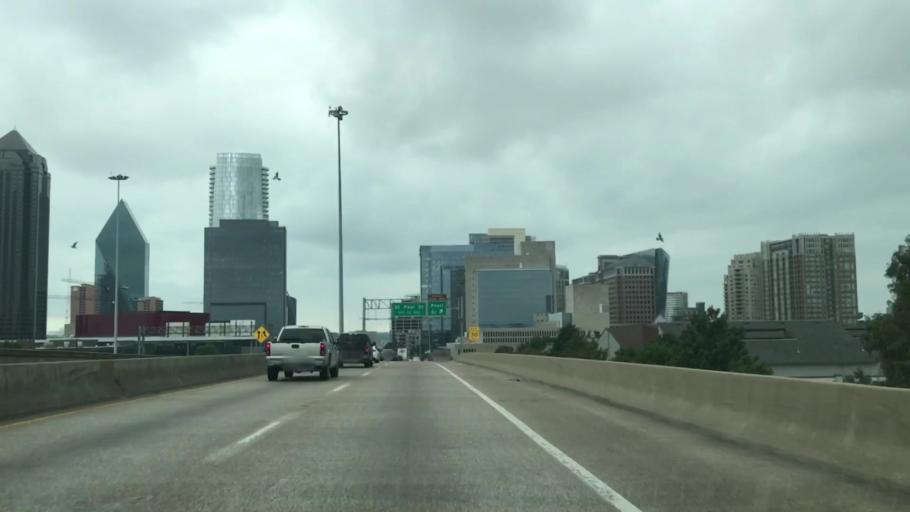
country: US
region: Texas
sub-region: Dallas County
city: Dallas
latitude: 32.7947
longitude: -96.7951
